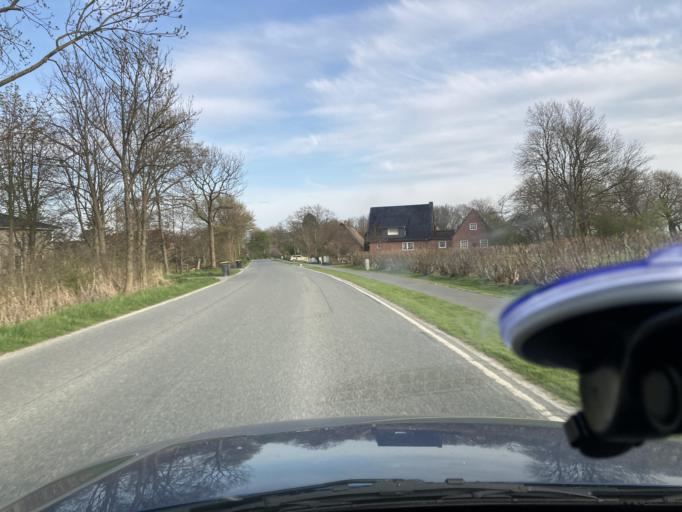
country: DE
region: Schleswig-Holstein
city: Strubbel
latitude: 54.2618
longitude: 8.9692
